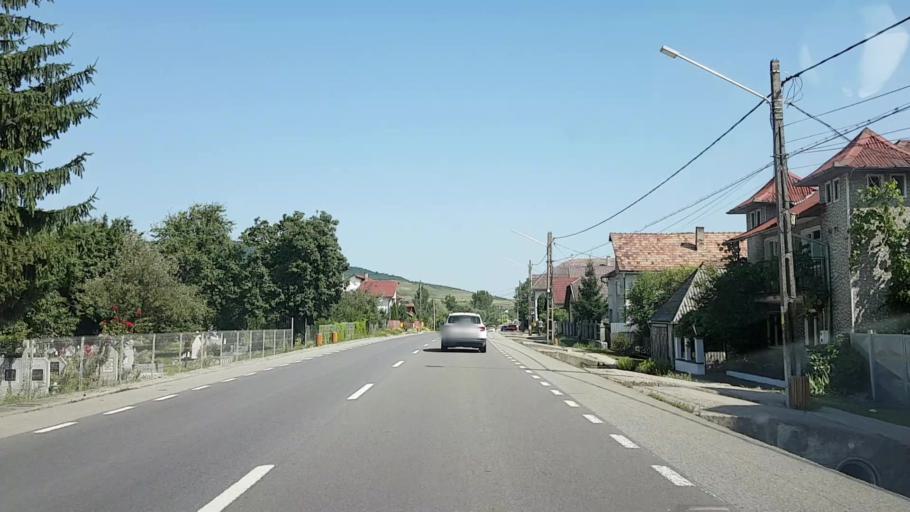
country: RO
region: Bistrita-Nasaud
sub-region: Comuna Sieu-Magherus
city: Sieu-Magherus
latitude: 47.0886
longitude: 24.3783
